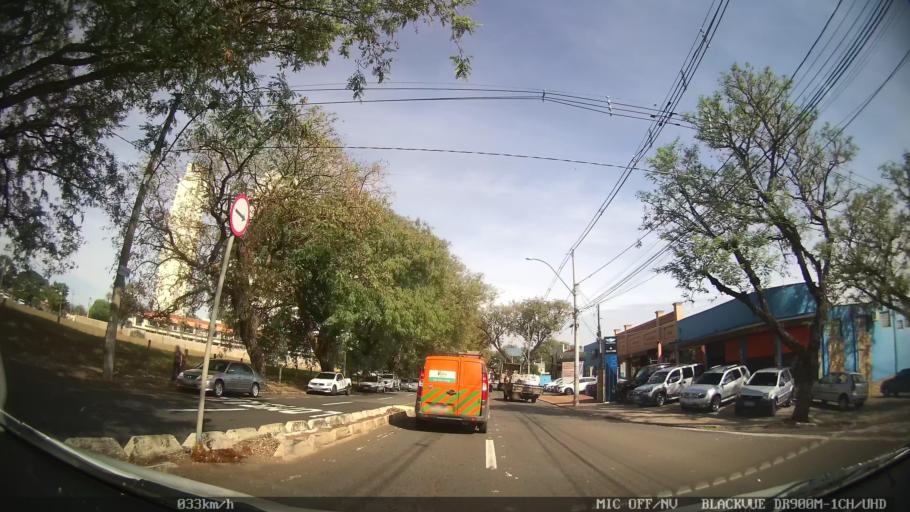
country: BR
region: Sao Paulo
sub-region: Piracicaba
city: Piracicaba
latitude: -22.7160
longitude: -47.6591
